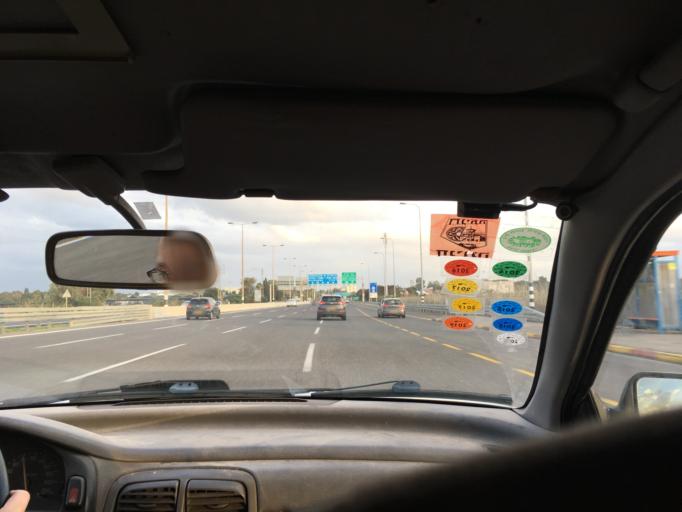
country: IL
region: Tel Aviv
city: Ramat HaSharon
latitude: 32.1386
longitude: 34.8199
